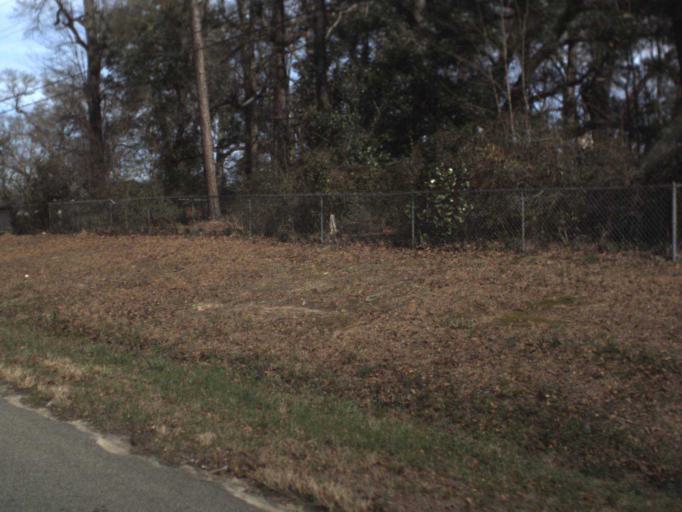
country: US
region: Florida
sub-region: Jackson County
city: Graceville
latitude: 30.9297
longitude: -85.5192
